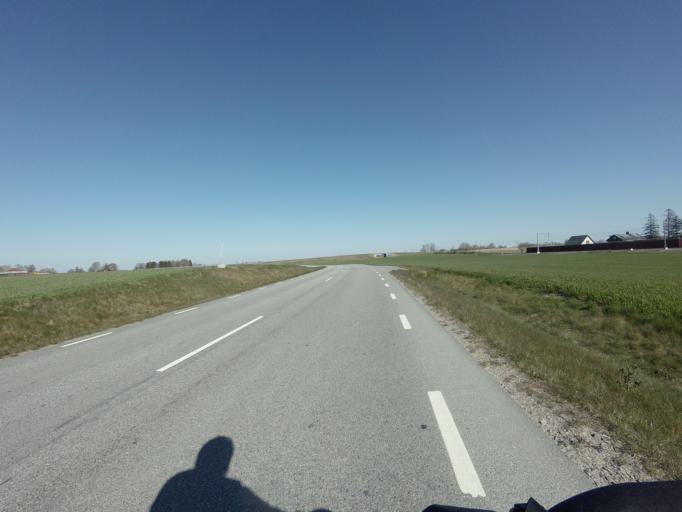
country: SE
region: Skane
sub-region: Malmo
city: Oxie
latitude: 55.4692
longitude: 13.1301
